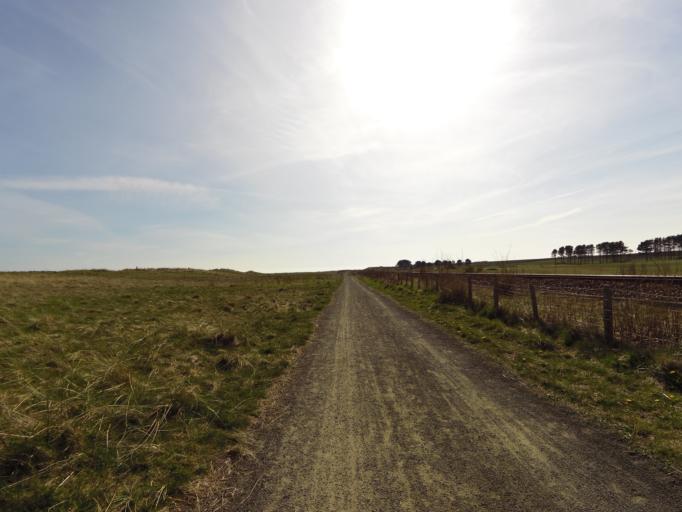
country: GB
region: Scotland
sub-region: Angus
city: Arbroath
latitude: 56.5332
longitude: -2.6324
